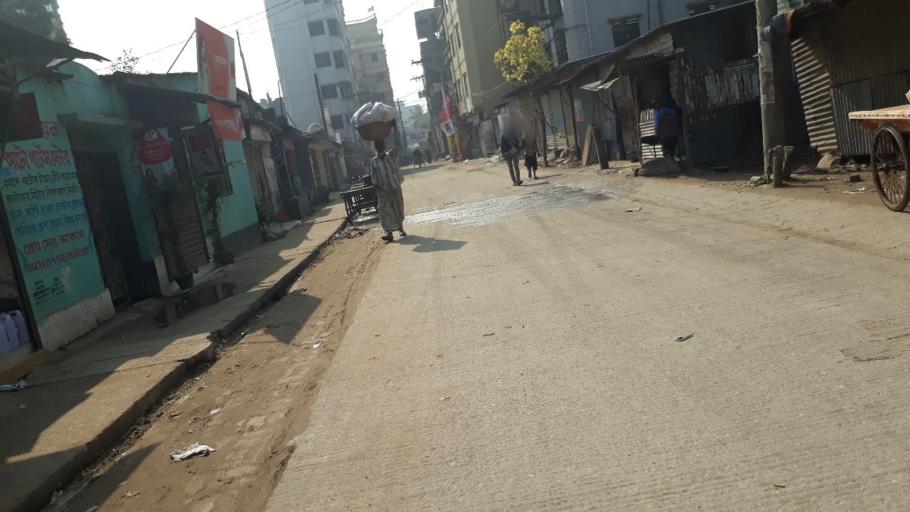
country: BD
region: Dhaka
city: Tungi
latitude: 23.8556
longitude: 90.2576
